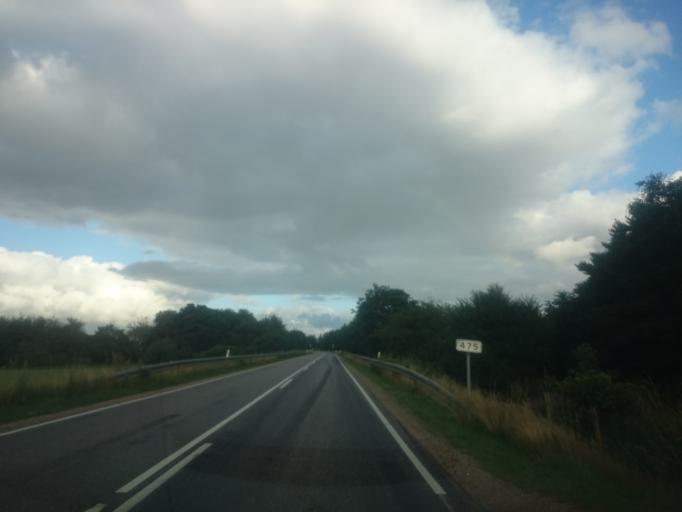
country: DK
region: South Denmark
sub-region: Varde Kommune
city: Olgod
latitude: 55.6669
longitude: 8.7362
